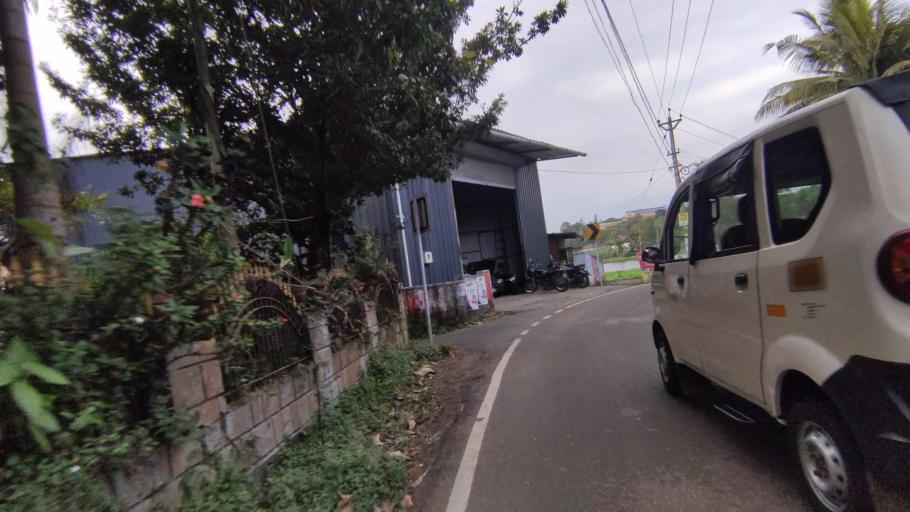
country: IN
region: Kerala
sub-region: Kottayam
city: Kottayam
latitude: 9.6392
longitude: 76.5161
